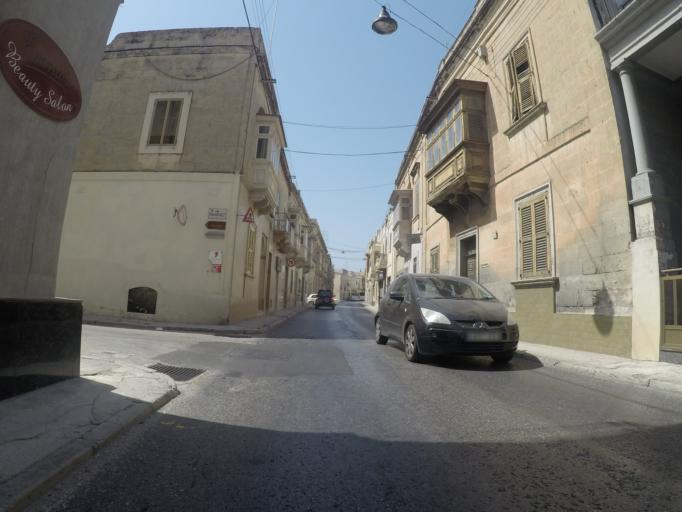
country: MT
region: Ir-Rabat
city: Rabat
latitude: 35.8790
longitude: 14.4007
